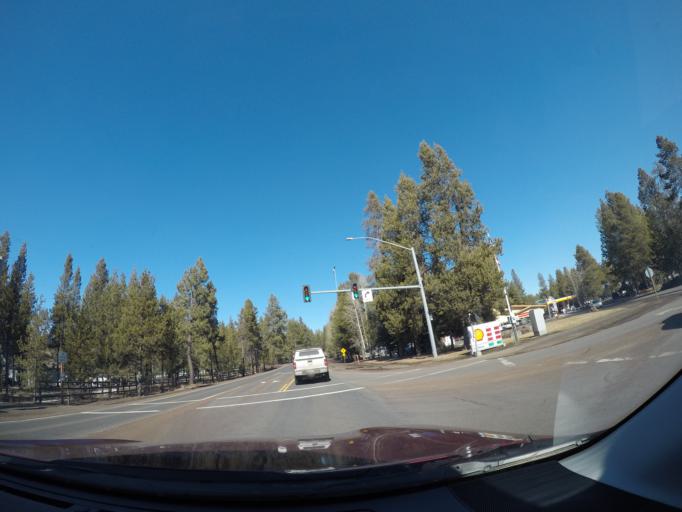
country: US
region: Oregon
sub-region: Deschutes County
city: Sunriver
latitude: 43.8662
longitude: -121.4369
